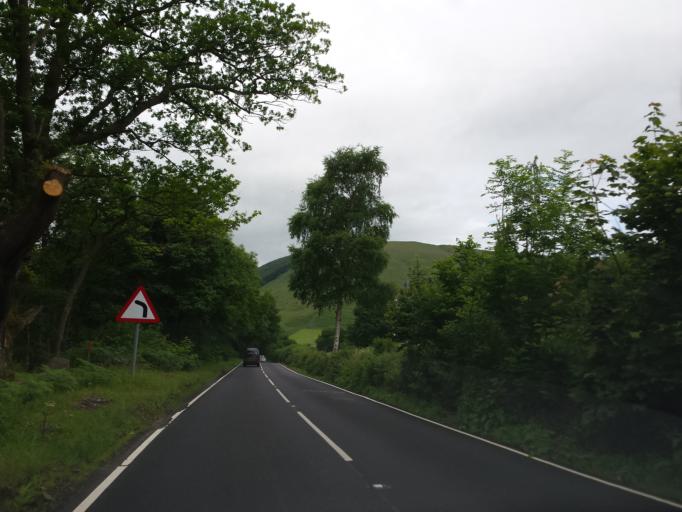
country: GB
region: Scotland
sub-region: Stirling
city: Callander
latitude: 56.3907
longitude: -4.2319
